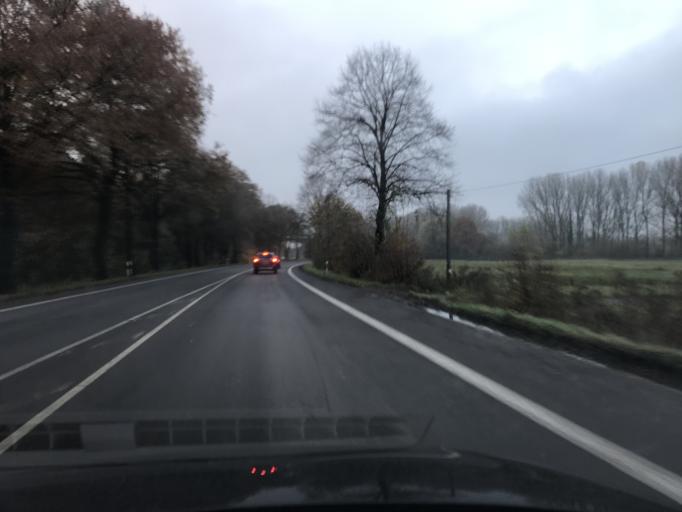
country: DE
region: North Rhine-Westphalia
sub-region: Regierungsbezirk Arnsberg
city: Welver
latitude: 51.6918
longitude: 7.9561
